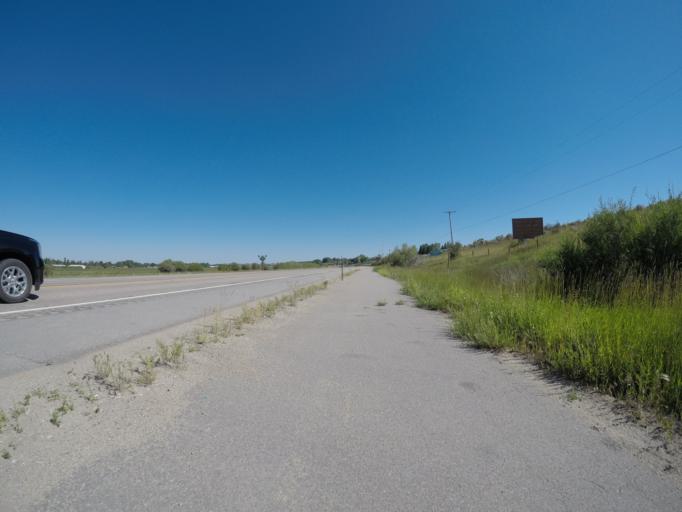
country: US
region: Wyoming
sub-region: Sublette County
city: Pinedale
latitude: 42.8536
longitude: -109.8504
